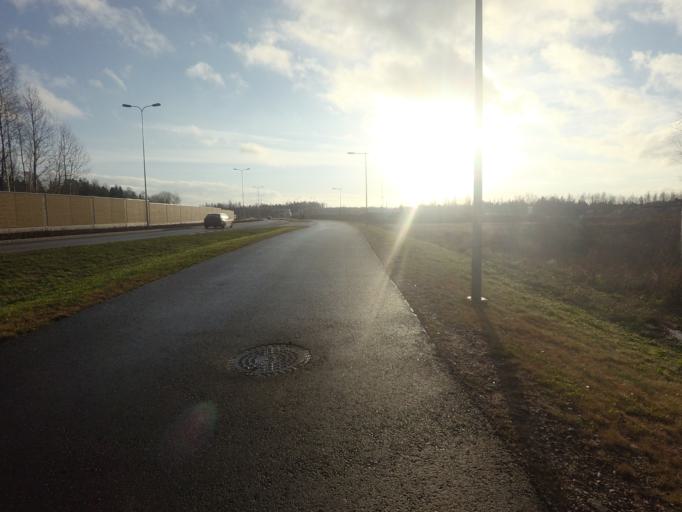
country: FI
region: Uusimaa
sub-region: Helsinki
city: Kilo
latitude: 60.2044
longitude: 24.7857
